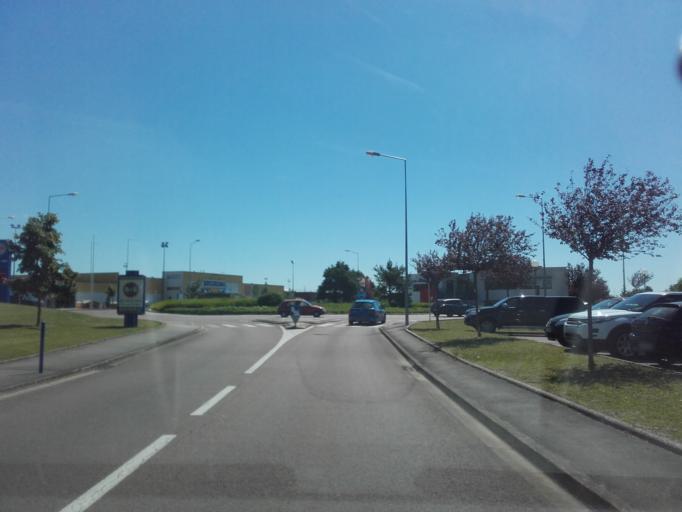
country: FR
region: Bourgogne
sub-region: Departement de la Cote-d'Or
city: Beaune
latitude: 47.0412
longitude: 4.8434
